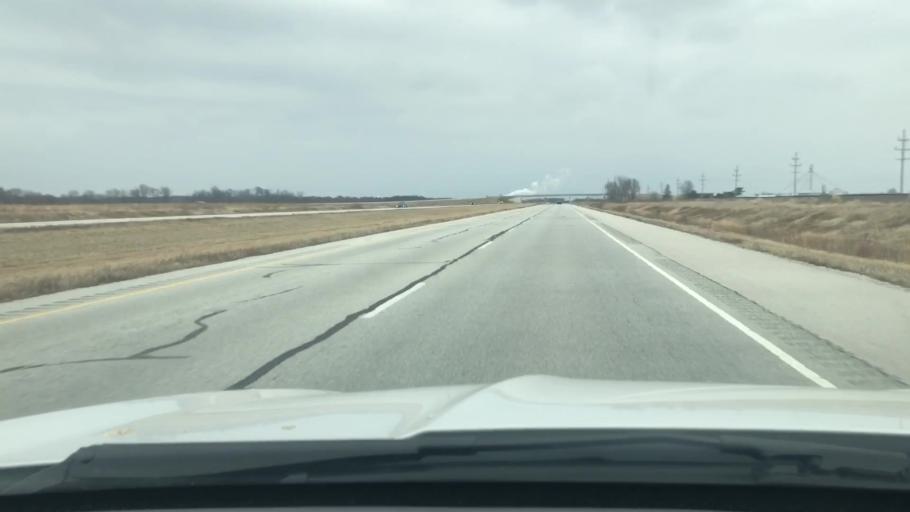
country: US
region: Indiana
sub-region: Cass County
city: Georgetown
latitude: 40.6873
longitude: -86.4879
